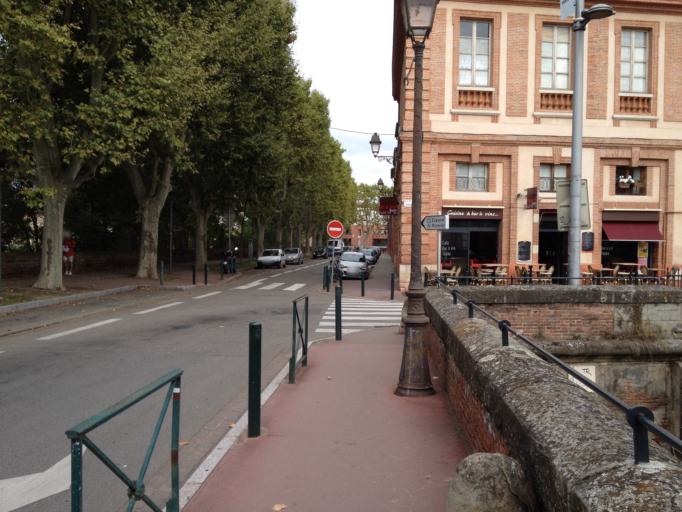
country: FR
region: Midi-Pyrenees
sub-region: Departement de la Haute-Garonne
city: Toulouse
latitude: 43.6039
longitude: 1.4341
